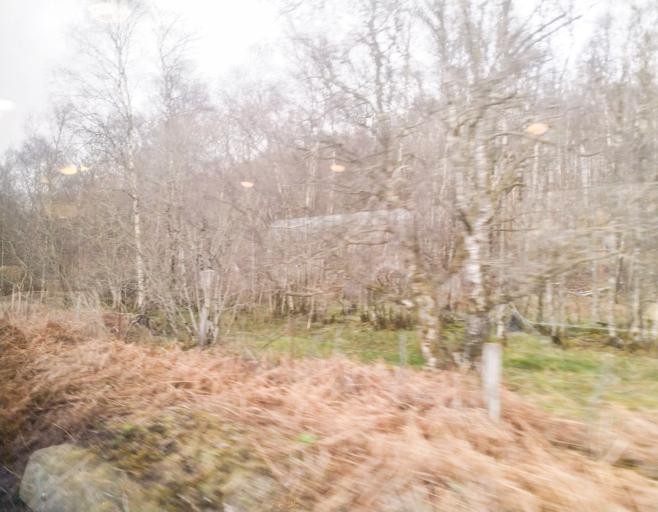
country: GB
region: Scotland
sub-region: Highland
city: Spean Bridge
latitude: 56.8857
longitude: -4.8181
